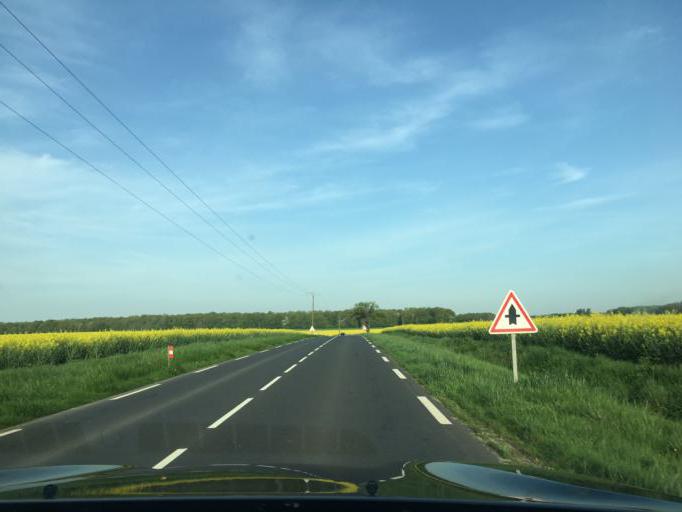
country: FR
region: Ile-de-France
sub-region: Departement des Yvelines
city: Gazeran
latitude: 48.5794
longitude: 1.7568
